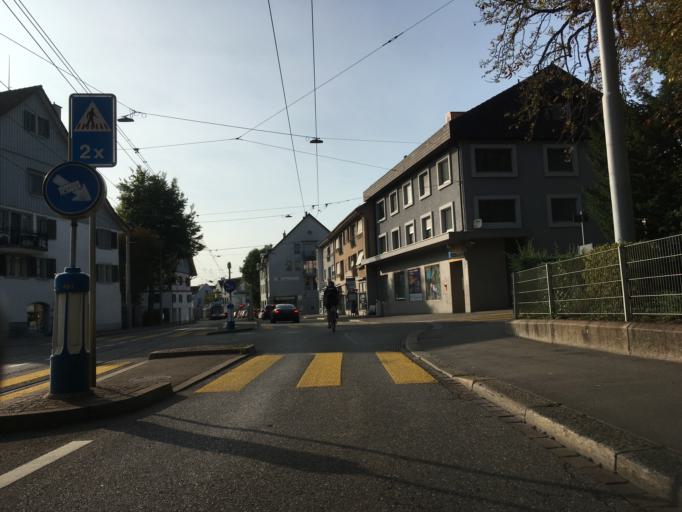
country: CH
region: Zurich
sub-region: Bezirk Zuerich
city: Zuerich (Kreis 10) / Hoengg
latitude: 47.4013
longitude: 8.5013
